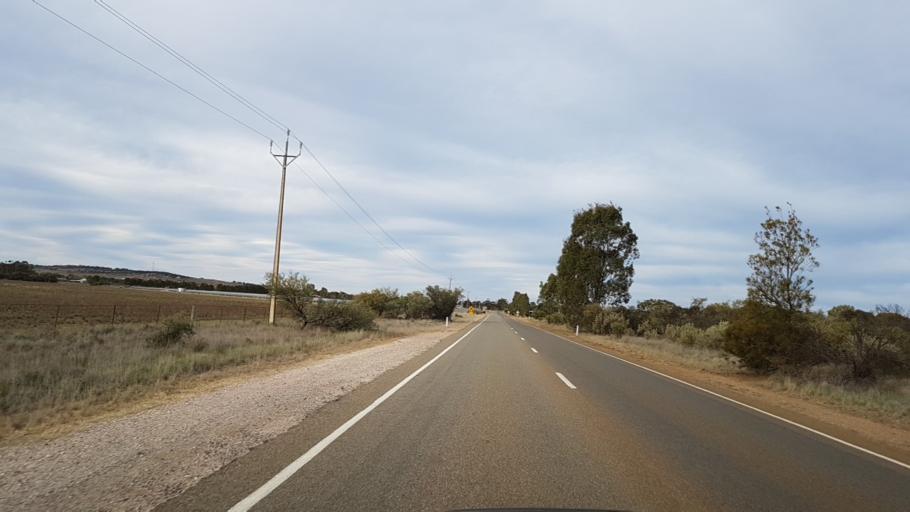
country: AU
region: South Australia
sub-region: Peterborough
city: Peterborough
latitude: -32.9823
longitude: 138.8110
